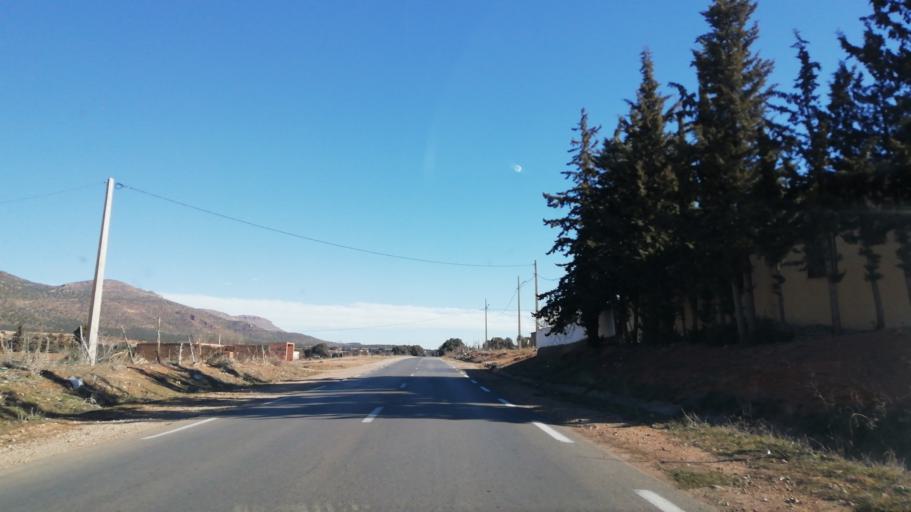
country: DZ
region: Tlemcen
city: Sebdou
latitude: 34.6900
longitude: -1.2434
